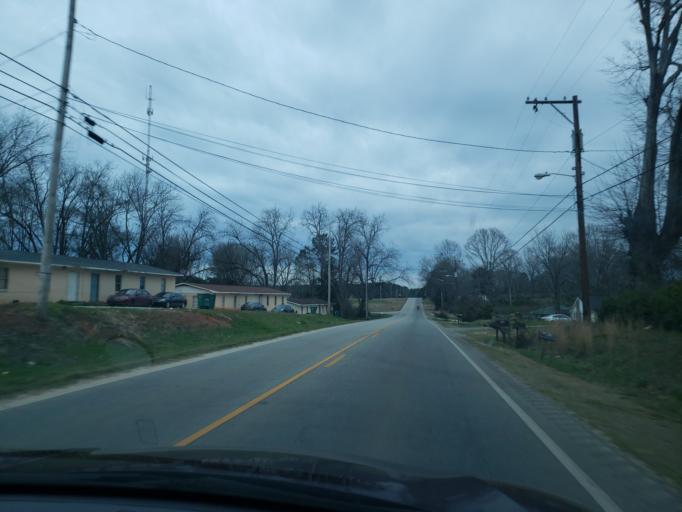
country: US
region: Alabama
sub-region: Chambers County
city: Lafayette
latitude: 32.9143
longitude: -85.4000
